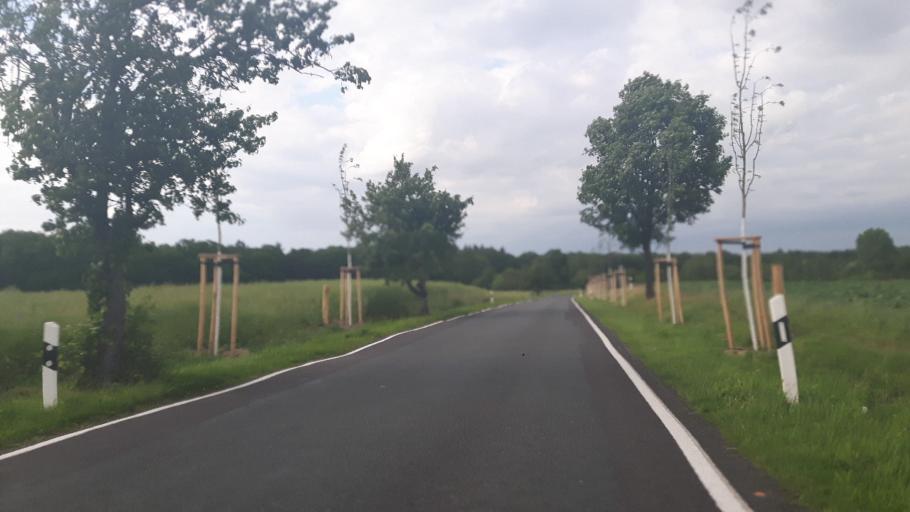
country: DE
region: Brandenburg
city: Hohenfinow
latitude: 52.7759
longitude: 13.8923
